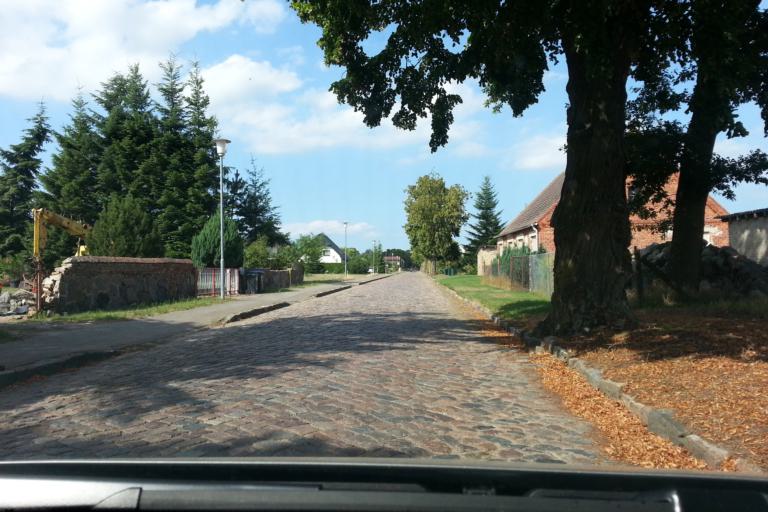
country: DE
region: Mecklenburg-Vorpommern
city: Ferdinandshof
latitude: 53.6393
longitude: 13.8715
